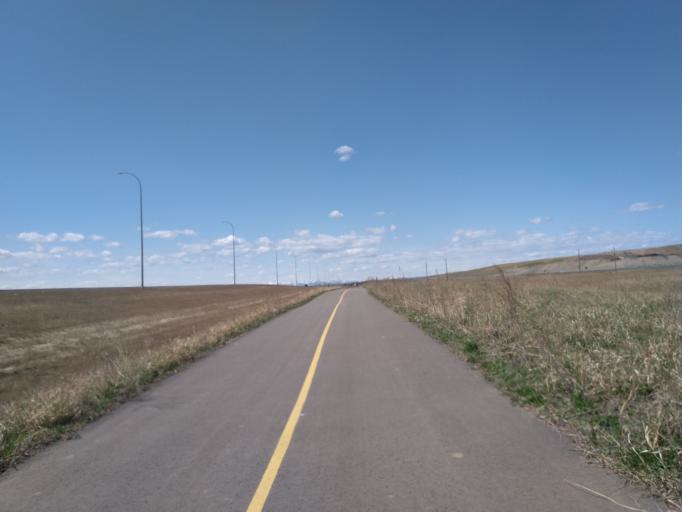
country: CA
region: Alberta
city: Chestermere
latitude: 51.0150
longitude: -113.9384
